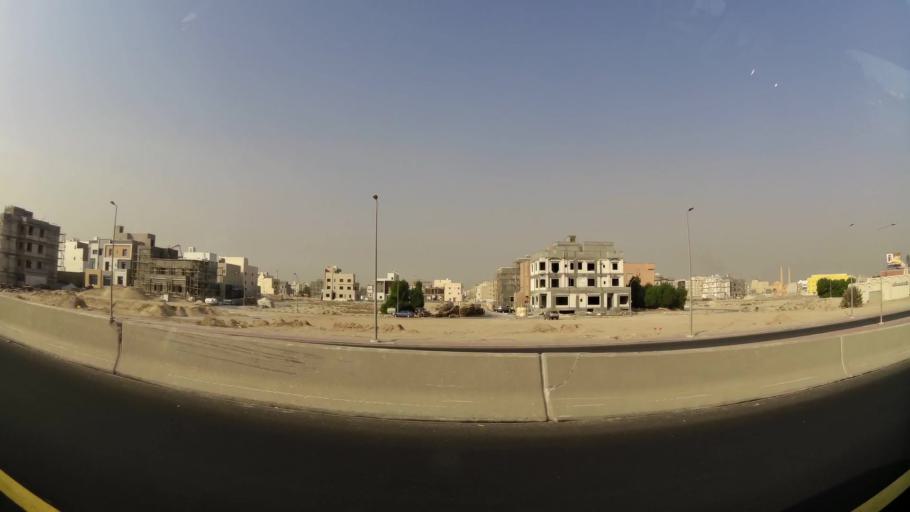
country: KW
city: Al Funaytis
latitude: 29.2158
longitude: 48.1021
